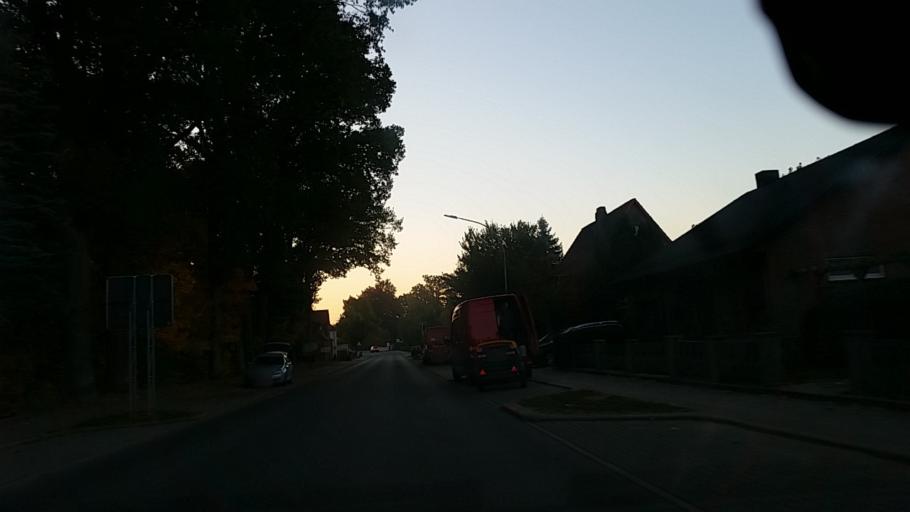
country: DE
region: Lower Saxony
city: Wieren
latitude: 52.8875
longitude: 10.6568
